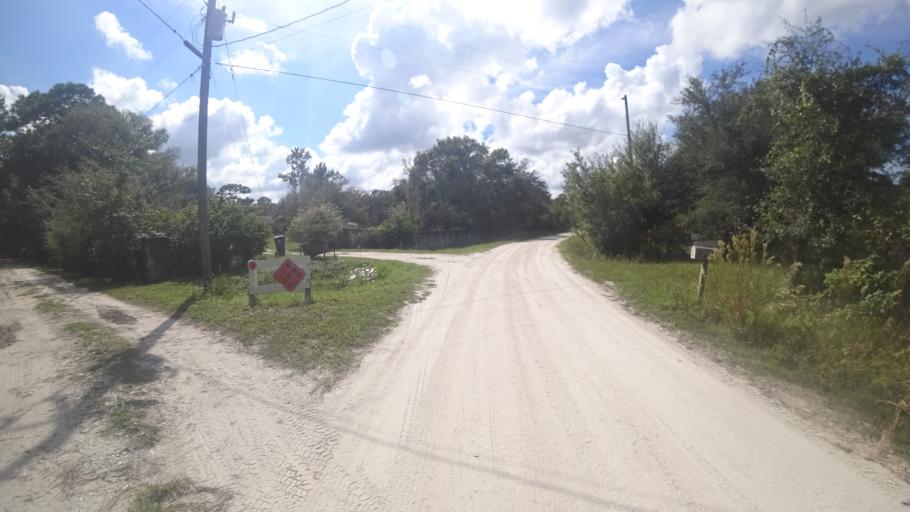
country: US
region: Florida
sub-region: Hillsborough County
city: Sun City Center
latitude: 27.6349
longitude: -82.3614
